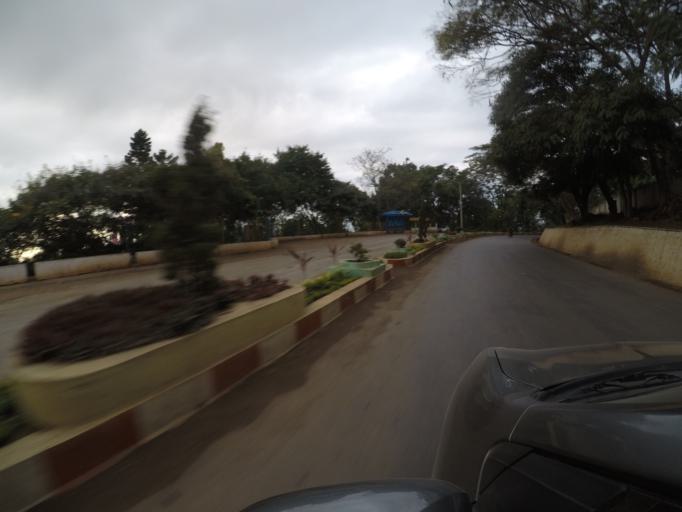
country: MM
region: Shan
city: Taunggyi
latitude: 20.8167
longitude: 97.0344
